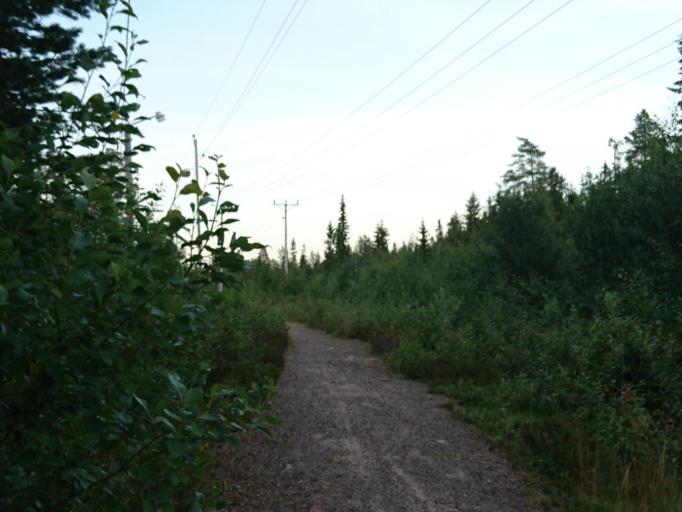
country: SE
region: Dalarna
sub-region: Malung-Saelens kommun
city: Malung
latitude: 61.1701
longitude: 13.1729
